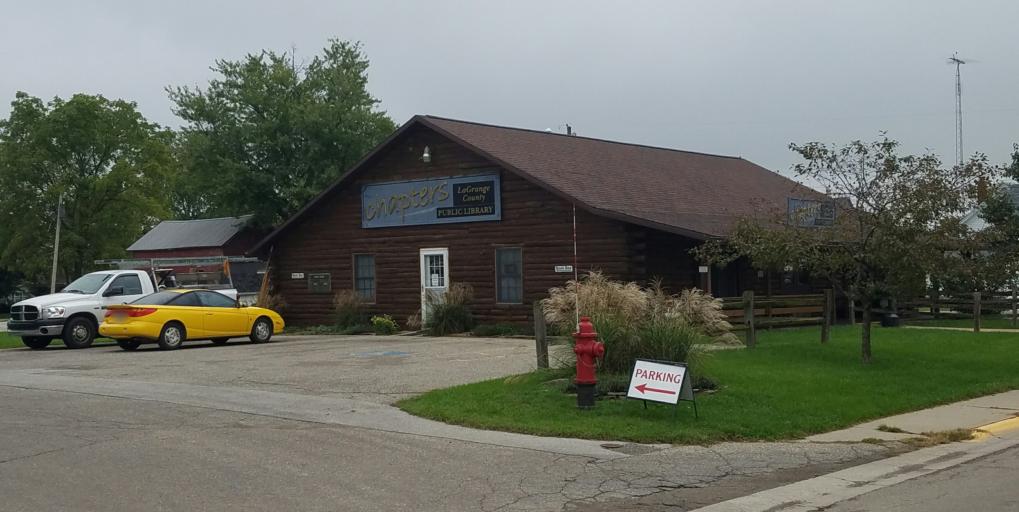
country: US
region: Indiana
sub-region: Elkhart County
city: Middlebury
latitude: 41.6786
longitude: -85.5801
